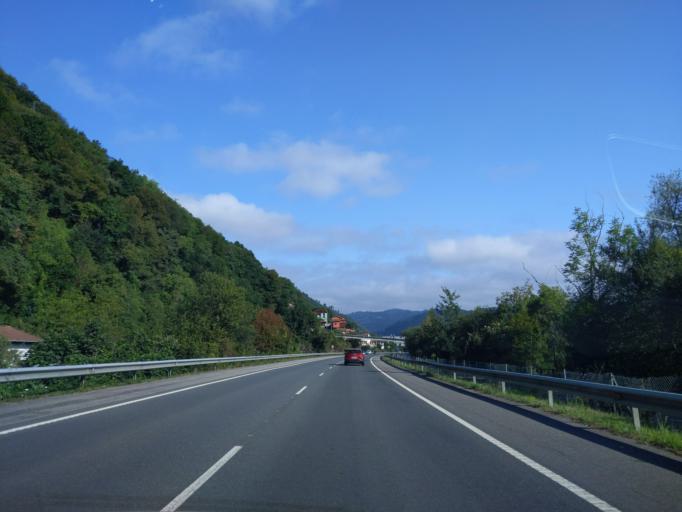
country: ES
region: Asturias
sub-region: Province of Asturias
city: Pola de Laviana
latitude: 43.2413
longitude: -5.5664
